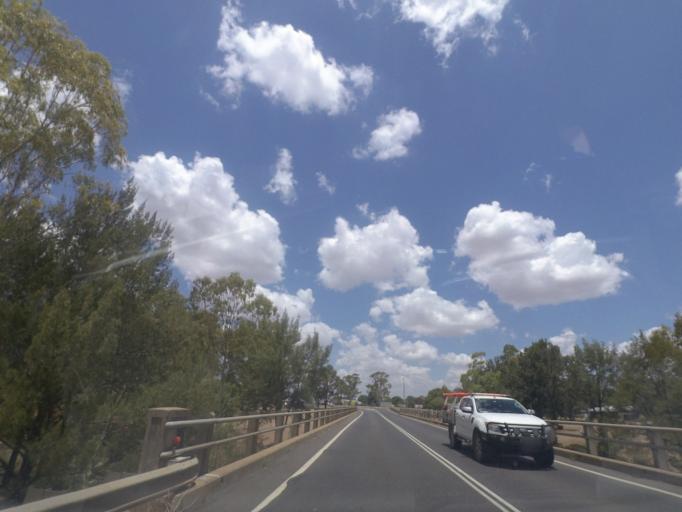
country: AU
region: Queensland
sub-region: Southern Downs
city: Warwick
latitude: -28.0344
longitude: 151.9877
